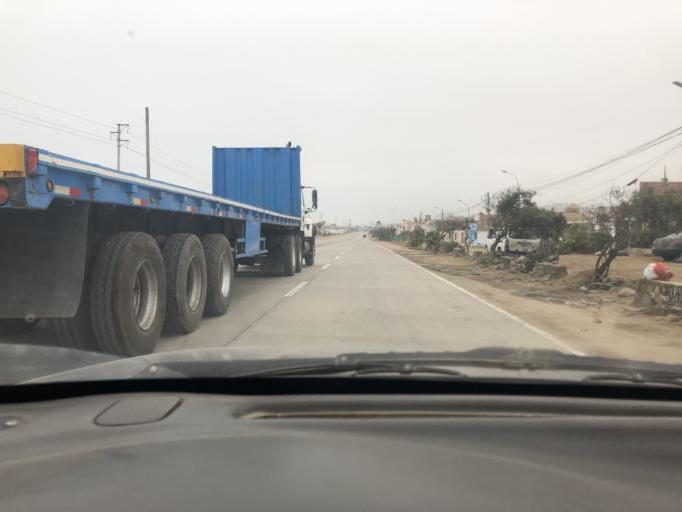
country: PE
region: Lima
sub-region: Lima
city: San Bartolo
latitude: -12.3727
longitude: -76.7868
